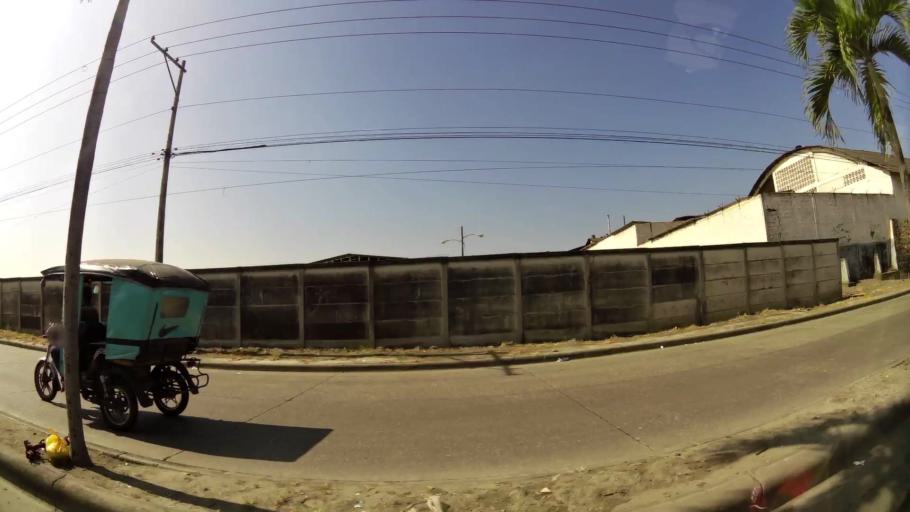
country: EC
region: Guayas
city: Eloy Alfaro
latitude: -2.1009
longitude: -79.9184
